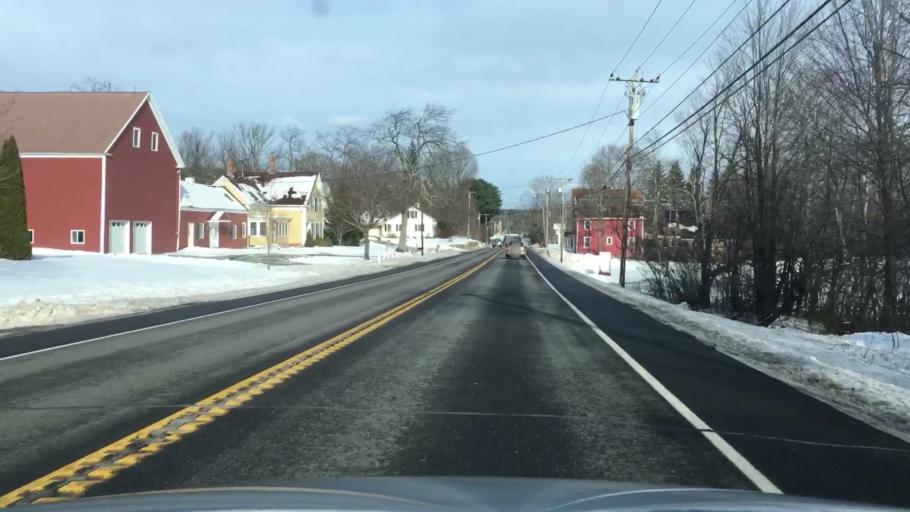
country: US
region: Maine
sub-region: Androscoggin County
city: Greene
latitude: 44.1760
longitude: -70.1705
